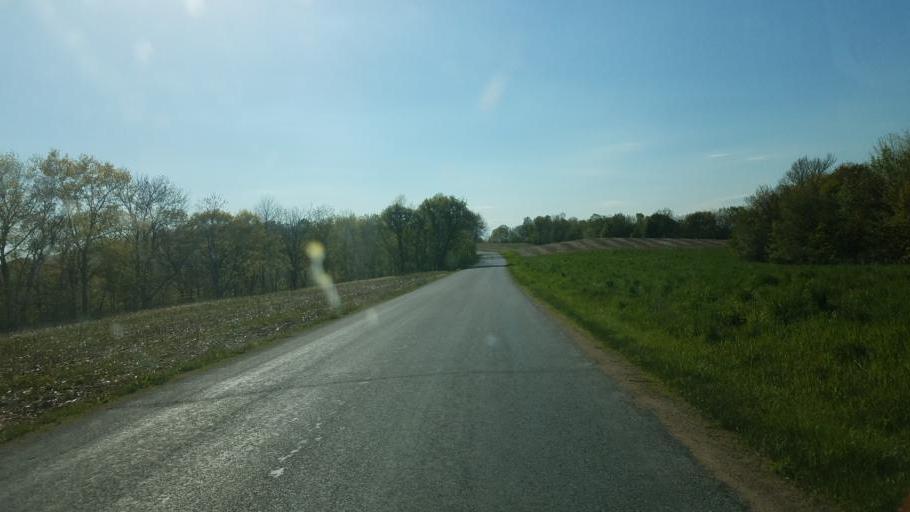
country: US
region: Wisconsin
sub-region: Vernon County
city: Hillsboro
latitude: 43.6744
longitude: -90.3588
